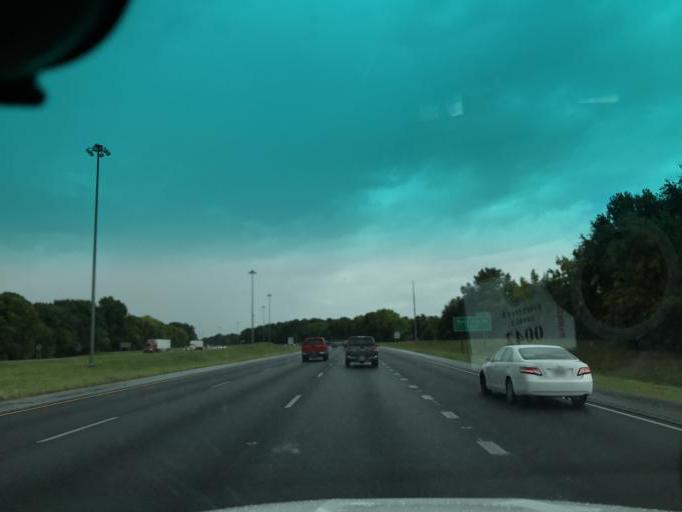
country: US
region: Alabama
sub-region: Montgomery County
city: Montgomery
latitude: 32.3621
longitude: -86.2626
